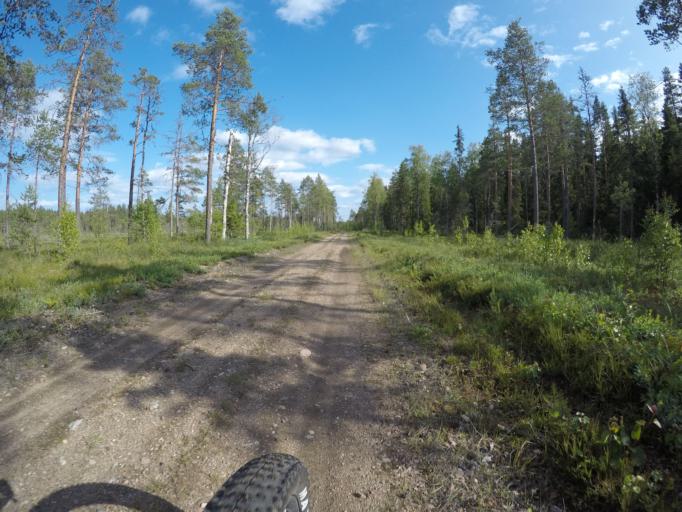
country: SE
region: OErebro
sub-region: Hallefors Kommun
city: Haellefors
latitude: 60.0825
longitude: 14.4997
